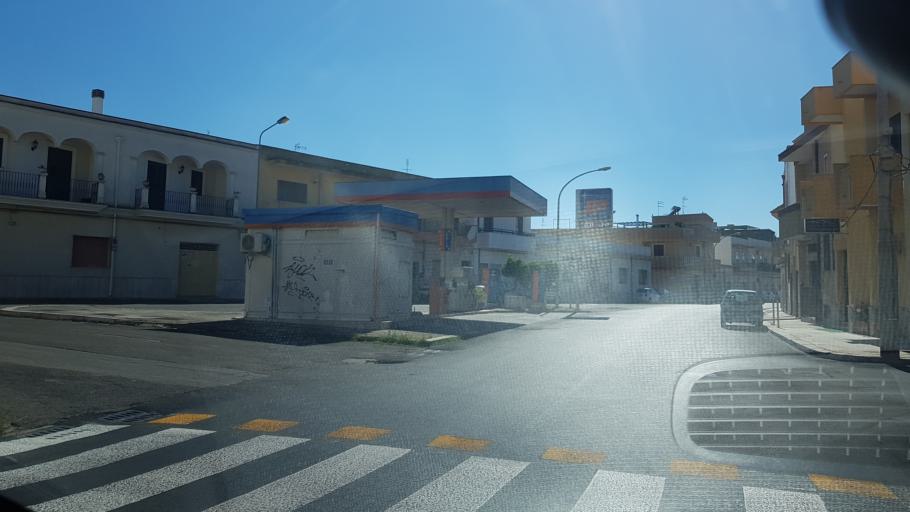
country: IT
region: Apulia
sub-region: Provincia di Brindisi
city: Mesagne
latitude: 40.5572
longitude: 17.8216
